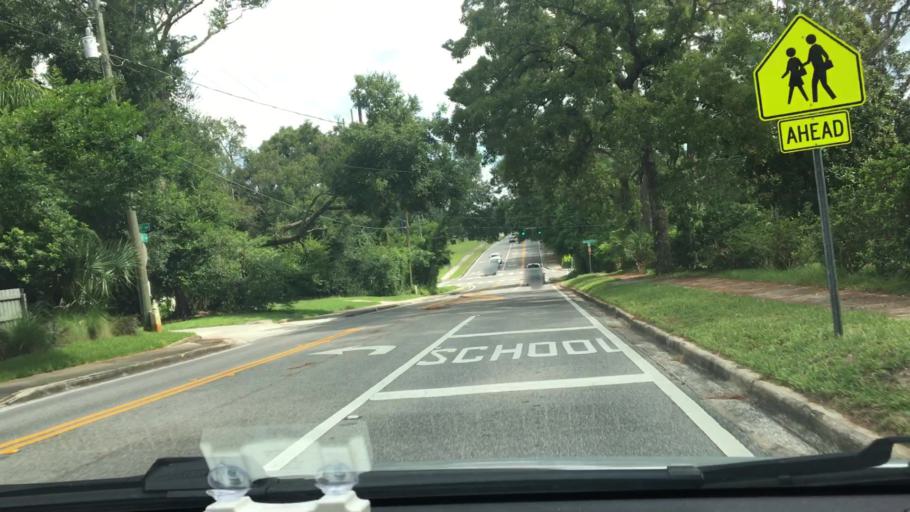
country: US
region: Florida
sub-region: Seminole County
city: Altamonte Springs
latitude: 28.6849
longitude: -81.3738
